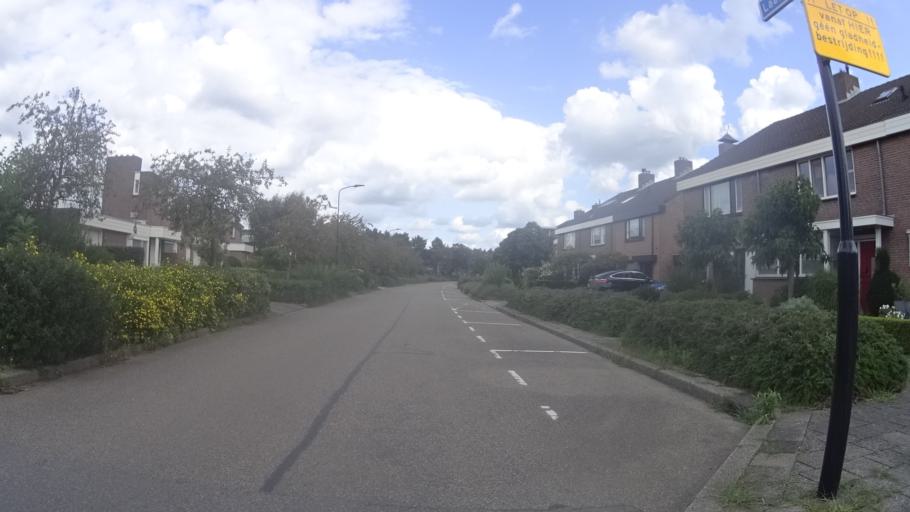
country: NL
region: North Holland
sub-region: Gemeente Beverwijk
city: Beverwijk
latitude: 52.4929
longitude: 4.6461
